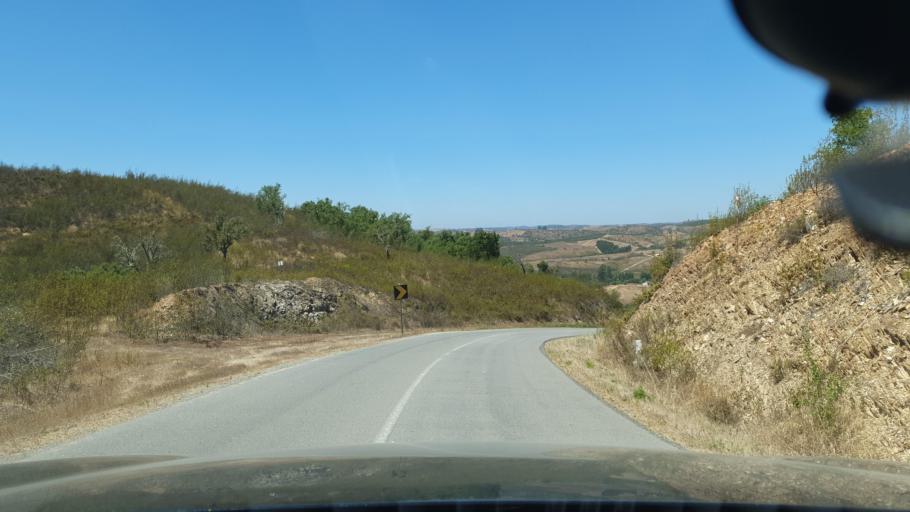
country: PT
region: Beja
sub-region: Odemira
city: Odemira
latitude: 37.5551
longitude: -8.4448
